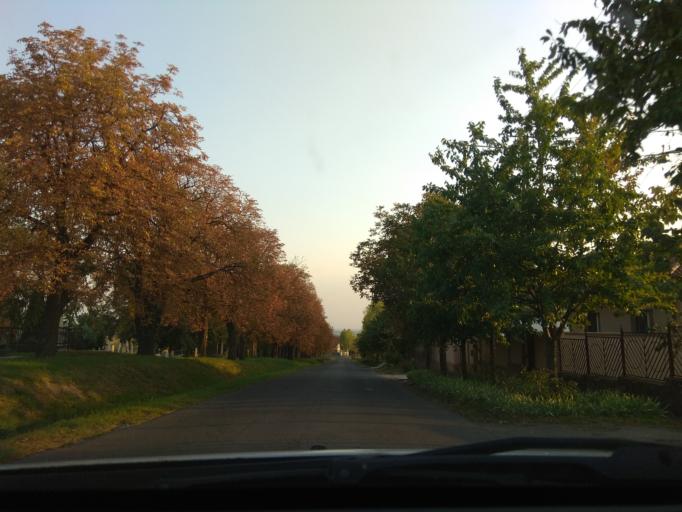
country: HU
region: Borsod-Abauj-Zemplen
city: Tallya
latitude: 48.2327
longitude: 21.2349
